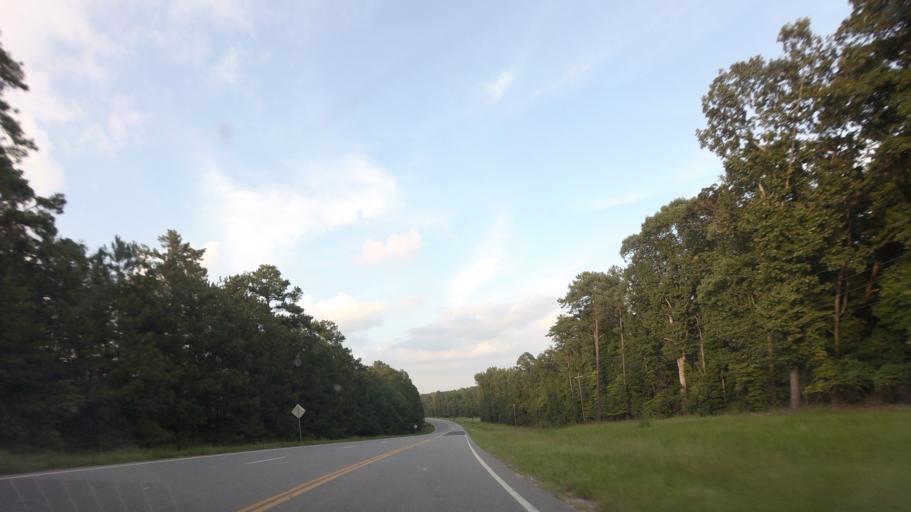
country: US
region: Georgia
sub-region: Wilkinson County
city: Gordon
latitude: 32.8653
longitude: -83.3459
